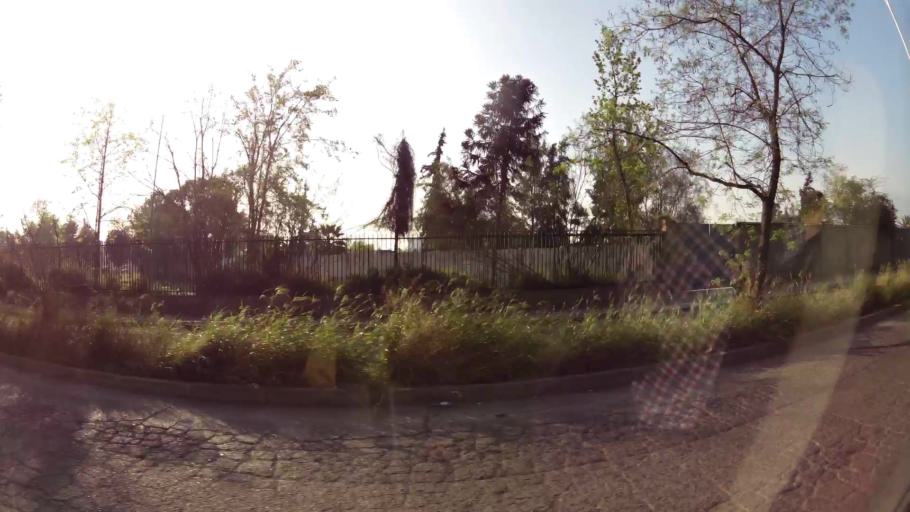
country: CL
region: Santiago Metropolitan
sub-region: Provincia de Santiago
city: Santiago
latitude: -33.4167
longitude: -70.6458
